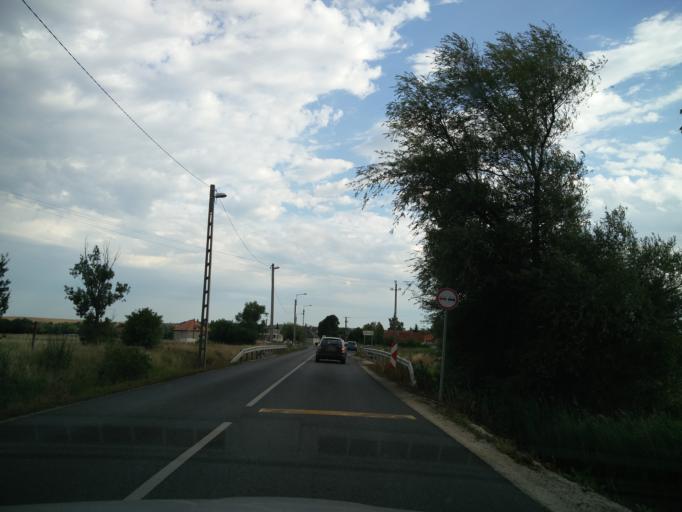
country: HU
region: Fejer
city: Zamoly
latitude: 47.3270
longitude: 18.4079
